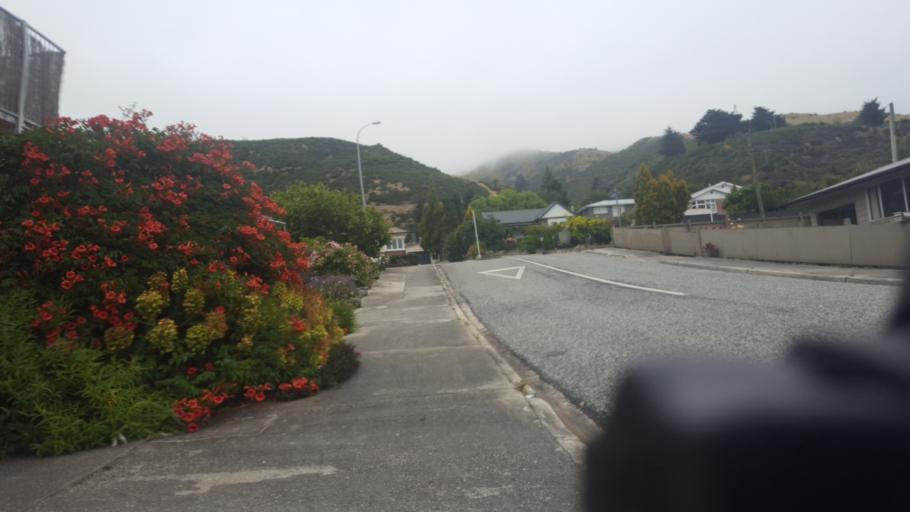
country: NZ
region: Otago
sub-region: Queenstown-Lakes District
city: Kingston
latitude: -45.5369
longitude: 169.3100
